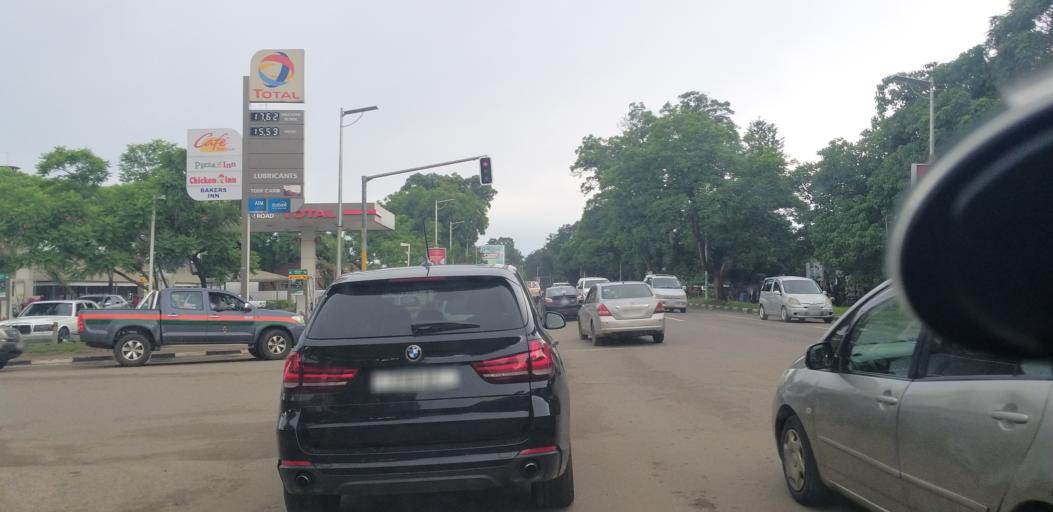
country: ZM
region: Lusaka
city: Lusaka
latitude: -15.4152
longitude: 28.2871
